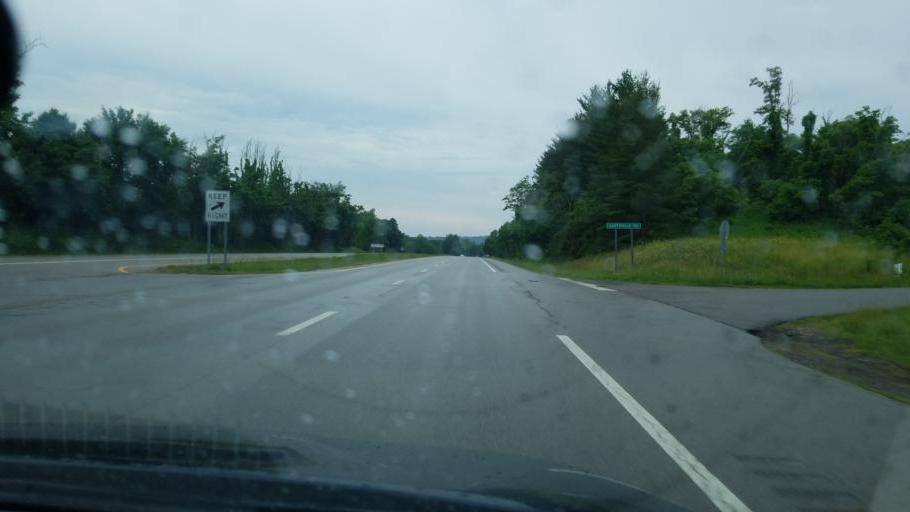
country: US
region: West Virginia
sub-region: Wood County
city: Washington
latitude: 39.2532
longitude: -81.7107
